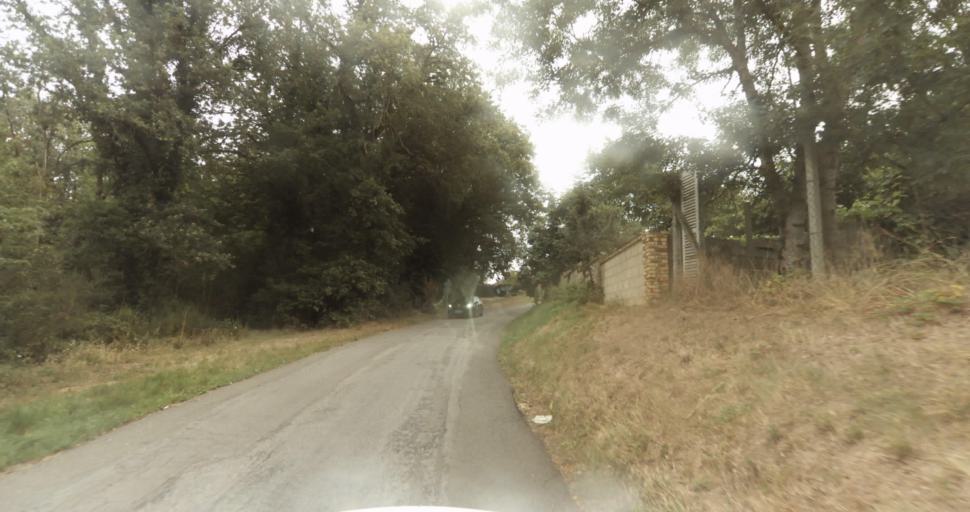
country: FR
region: Haute-Normandie
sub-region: Departement de l'Eure
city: Saint-Germain-sur-Avre
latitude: 48.7684
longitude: 1.2636
